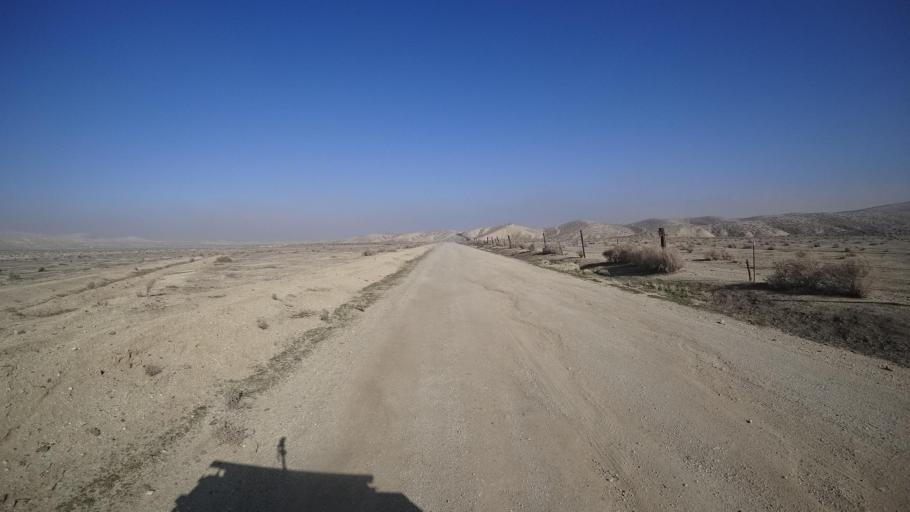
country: US
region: California
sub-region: Kern County
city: Maricopa
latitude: 35.0372
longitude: -119.4336
